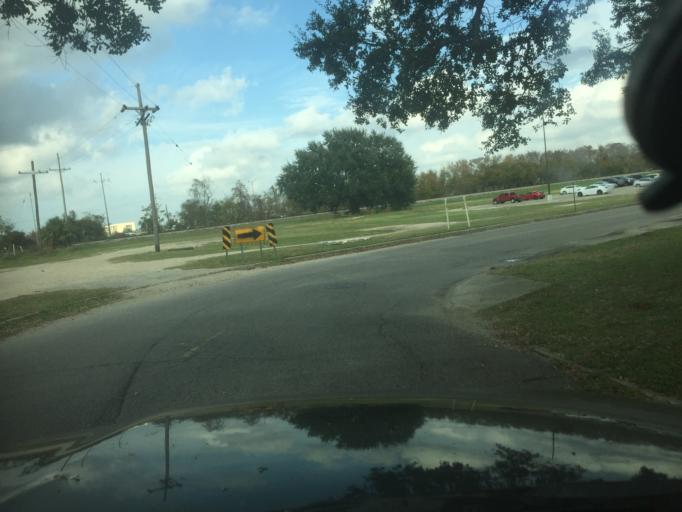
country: US
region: Louisiana
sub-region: Orleans Parish
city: New Orleans
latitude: 29.9916
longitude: -90.0862
